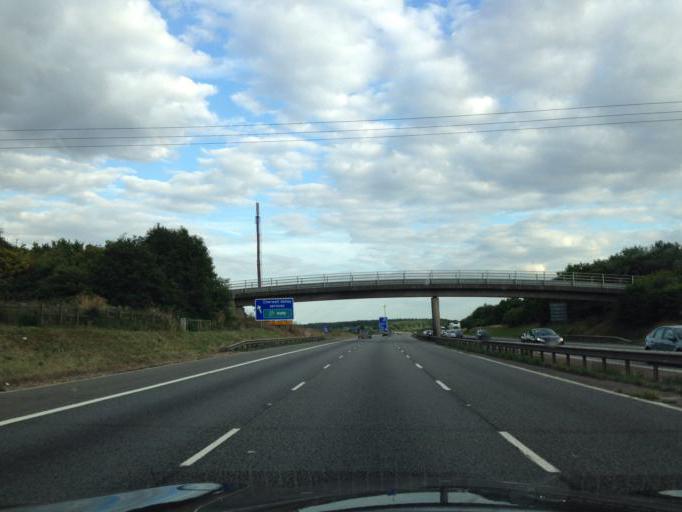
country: GB
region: England
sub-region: Oxfordshire
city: Somerton
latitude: 51.9587
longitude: -1.2158
